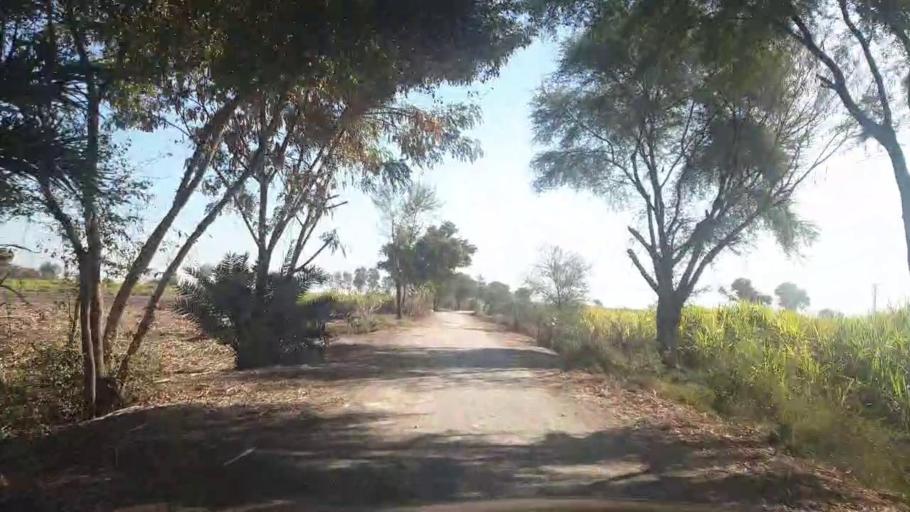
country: PK
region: Sindh
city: Adilpur
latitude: 27.9689
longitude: 69.3342
